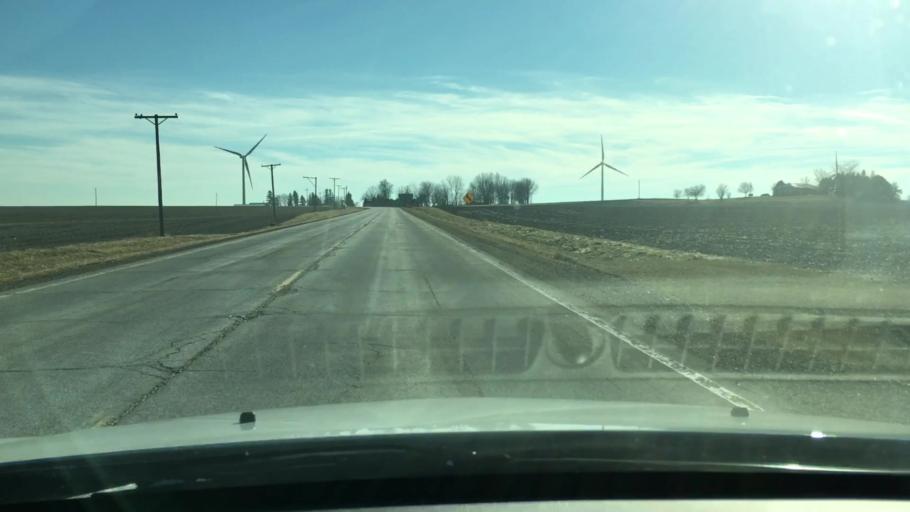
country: US
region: Illinois
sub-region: LaSalle County
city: Mendota
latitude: 41.6316
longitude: -89.1295
